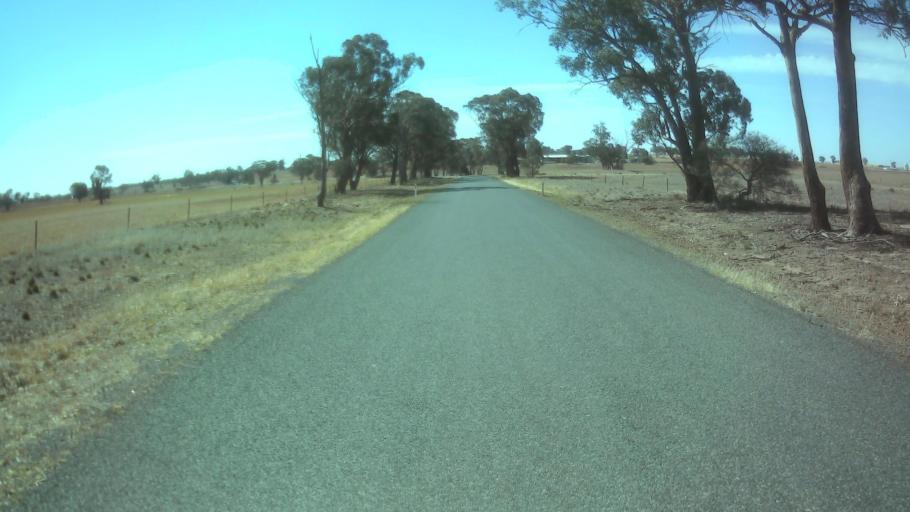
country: AU
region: New South Wales
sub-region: Weddin
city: Grenfell
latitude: -33.7661
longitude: 147.8649
